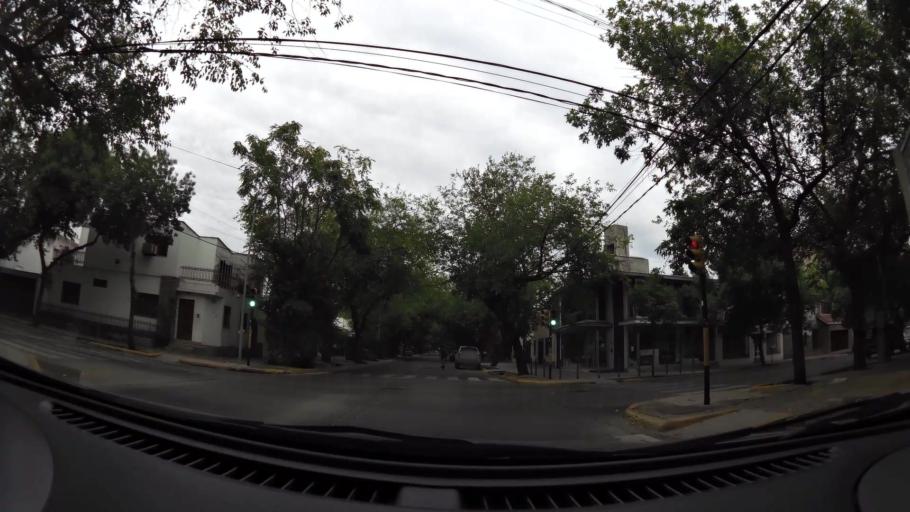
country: AR
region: Mendoza
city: Mendoza
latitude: -32.9022
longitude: -68.8517
